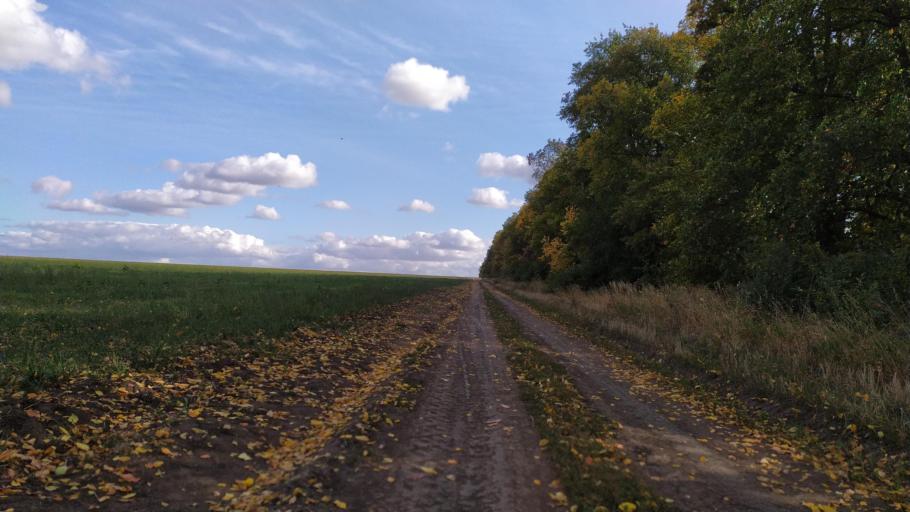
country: RU
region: Kursk
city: Kursk
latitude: 51.6206
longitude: 36.1620
